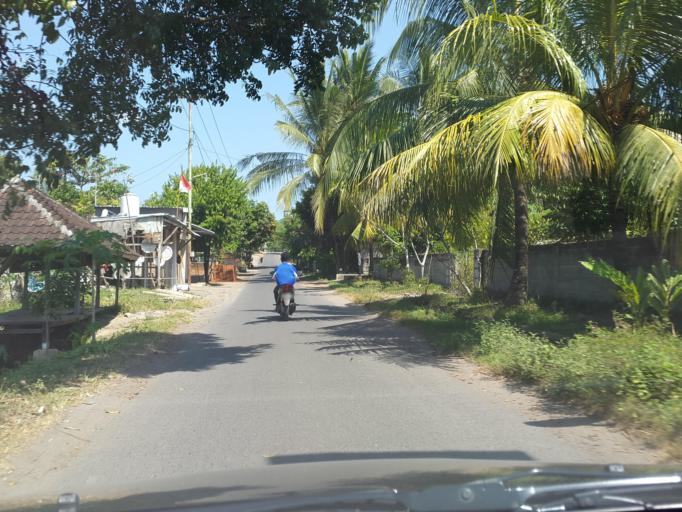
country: ID
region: West Nusa Tenggara
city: Mambalan
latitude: -8.5498
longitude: 116.1304
